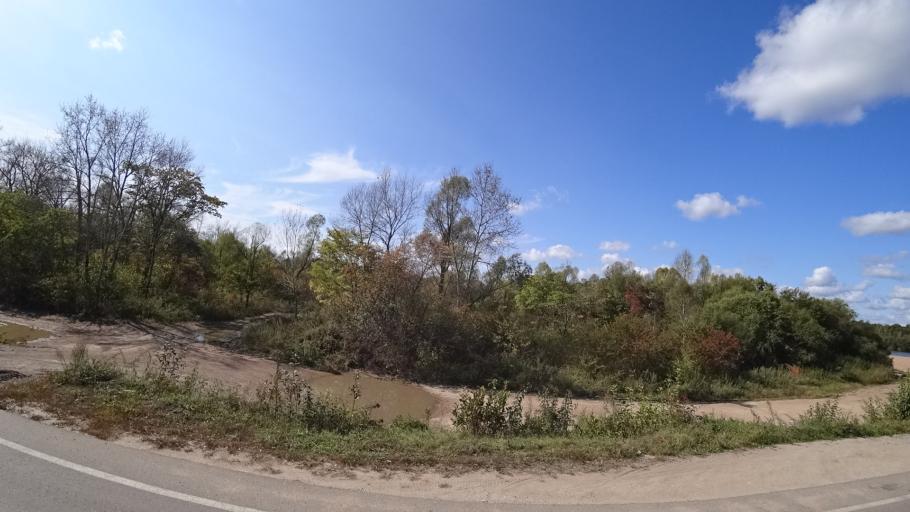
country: RU
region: Amur
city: Arkhara
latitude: 49.3963
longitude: 130.1345
